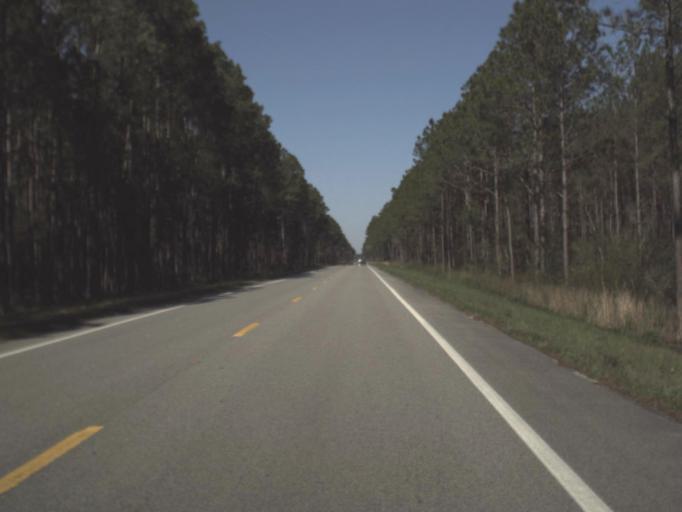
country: US
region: Florida
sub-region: Gulf County
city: Wewahitchka
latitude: 29.9498
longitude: -85.1821
